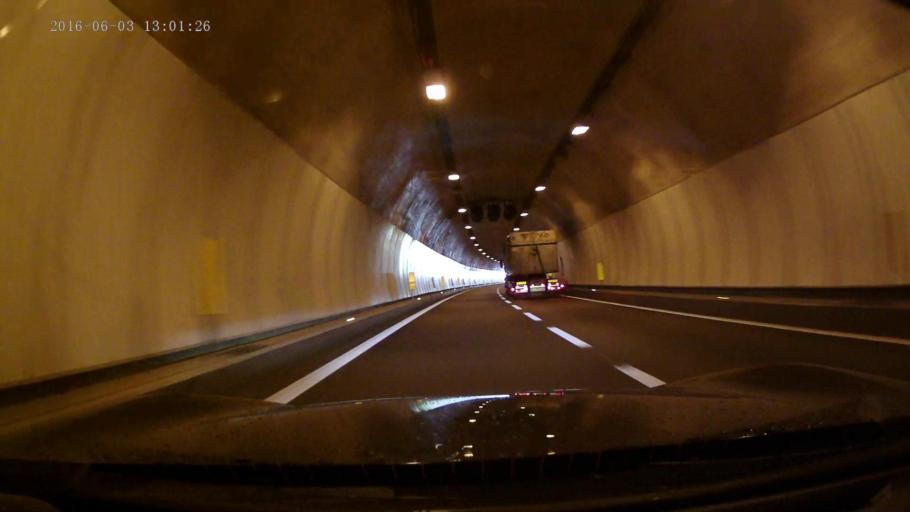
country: IT
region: Trentino-Alto Adige
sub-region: Bolzano
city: Fortezza
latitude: 46.7875
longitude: 11.6147
